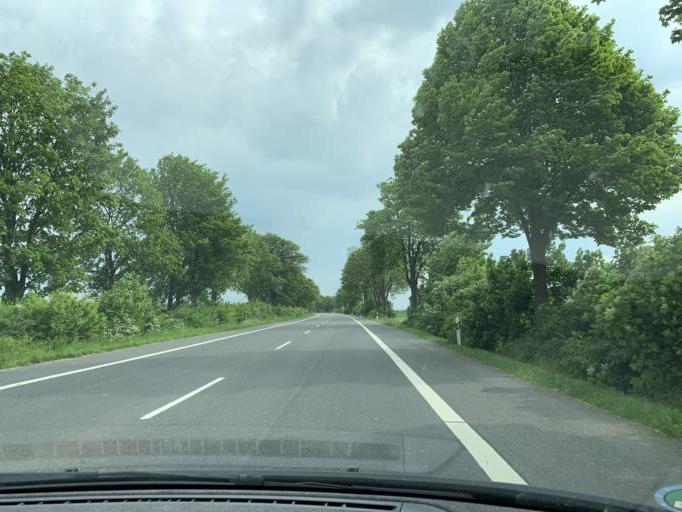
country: DE
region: North Rhine-Westphalia
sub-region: Regierungsbezirk Koln
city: Norvenich
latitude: 50.7925
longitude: 6.6354
